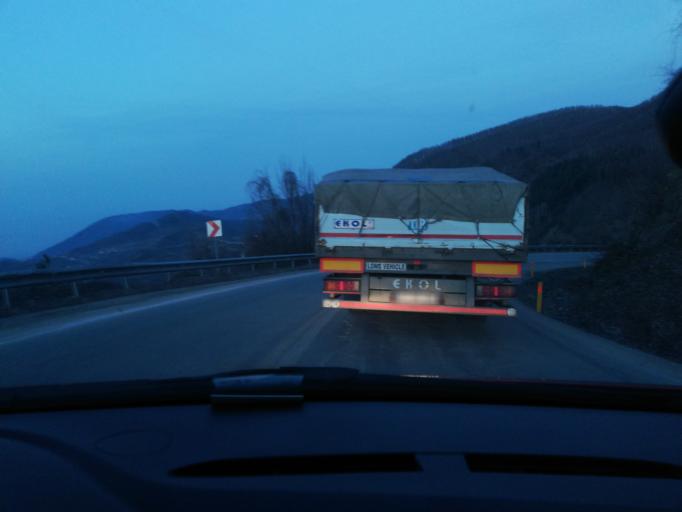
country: TR
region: Kastamonu
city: Inebolu
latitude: 41.9174
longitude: 33.7279
